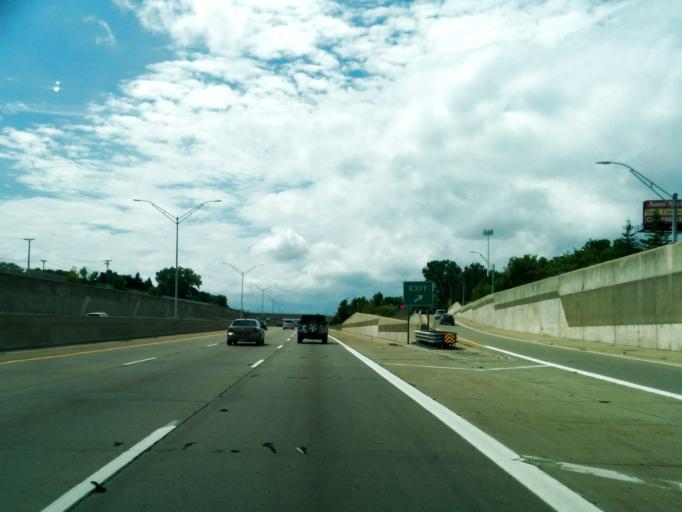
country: US
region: Michigan
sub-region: Macomb County
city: Utica
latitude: 42.6252
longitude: -83.0425
